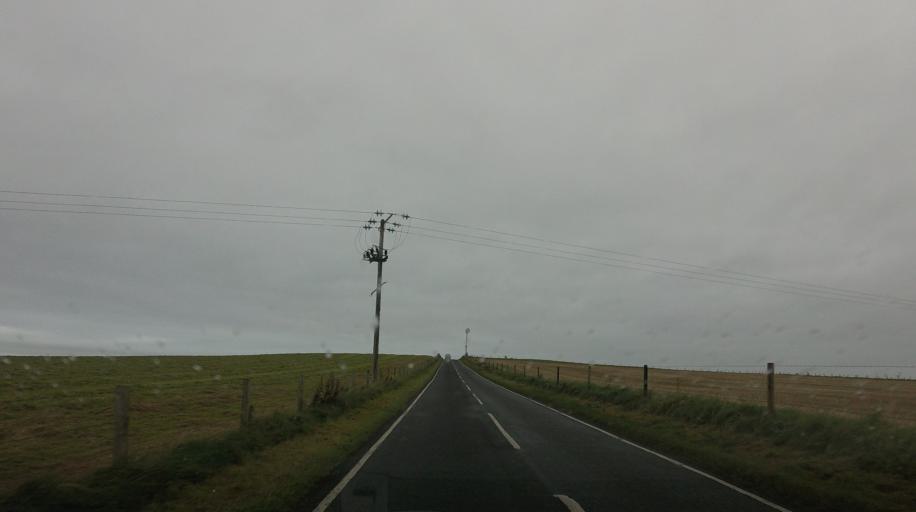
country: GB
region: Scotland
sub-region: Orkney Islands
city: Stromness
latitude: 59.1284
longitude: -3.3023
